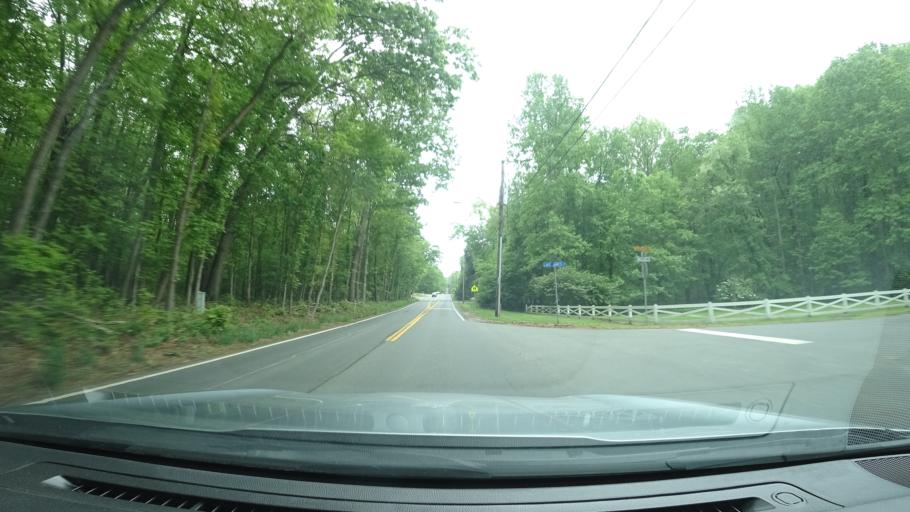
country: US
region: Virginia
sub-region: Fairfax County
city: Oak Hill
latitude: 38.9158
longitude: -77.3659
